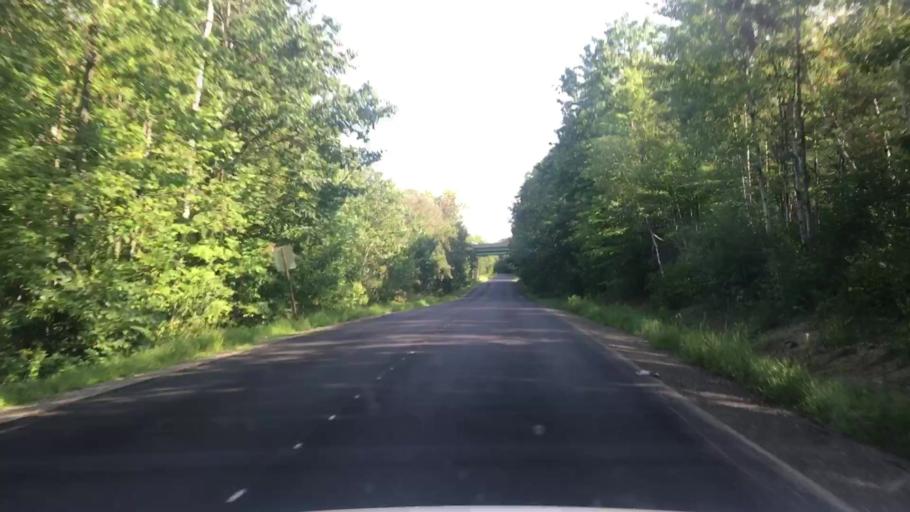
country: US
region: Maine
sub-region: Kennebec County
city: Waterville
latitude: 44.5735
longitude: -69.6577
